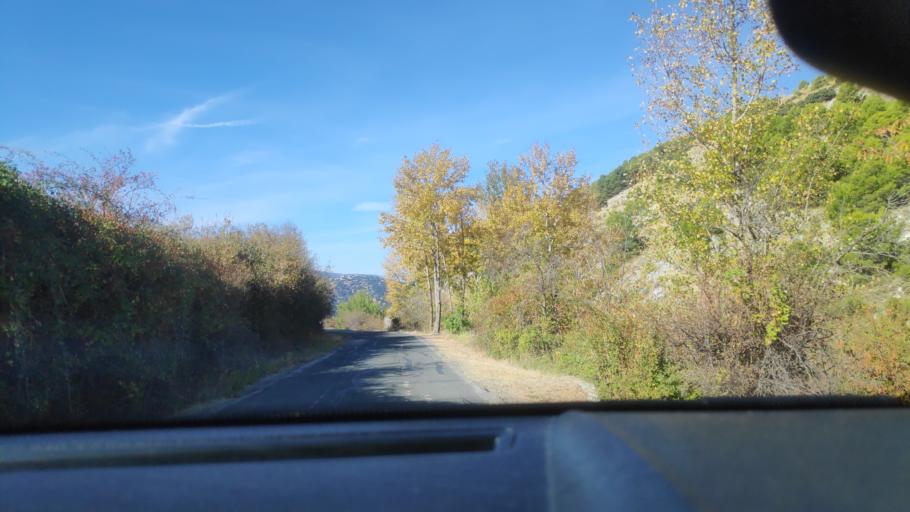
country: ES
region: Andalusia
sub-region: Provincia de Jaen
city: Torres
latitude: 37.7856
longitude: -3.4911
